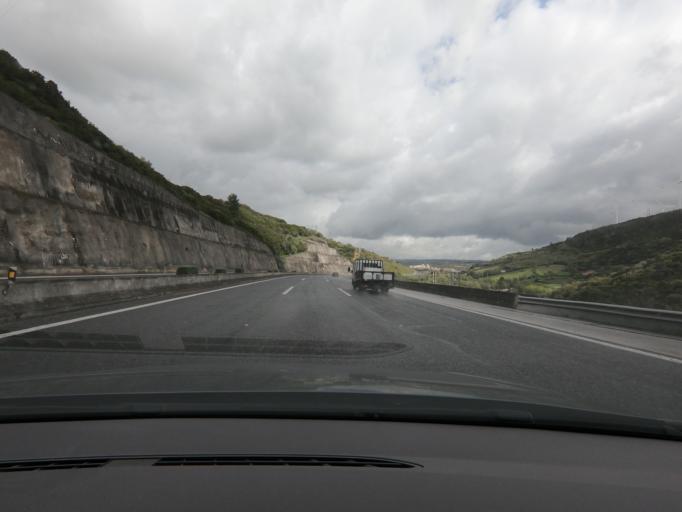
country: PT
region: Lisbon
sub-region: Loures
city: Bucelas
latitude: 38.8823
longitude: -9.1298
